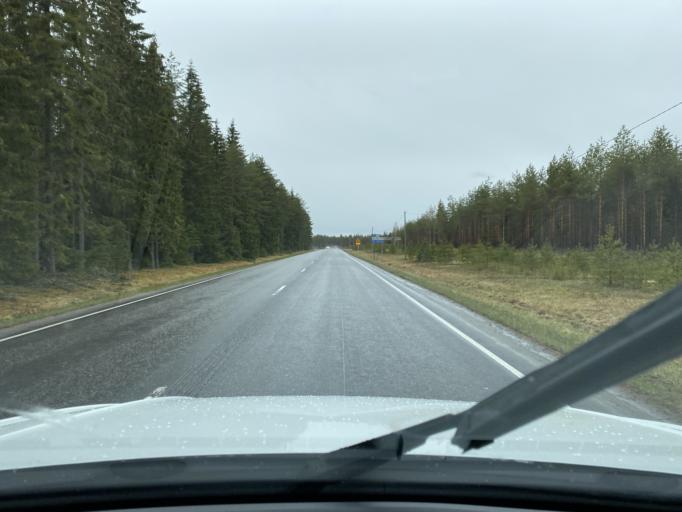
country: FI
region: Satakunta
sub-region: Pori
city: Vampula
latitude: 60.9530
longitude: 22.6706
